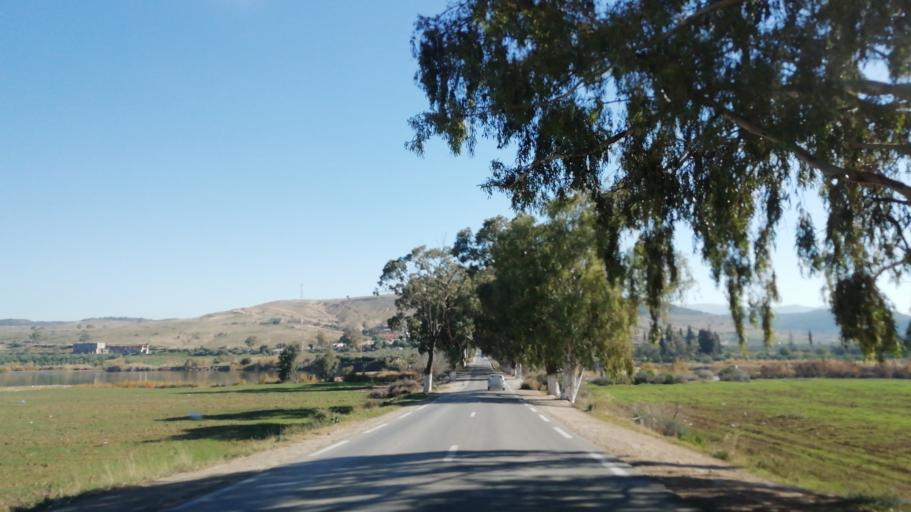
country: DZ
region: Tlemcen
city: Nedroma
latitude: 34.8271
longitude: -1.6574
